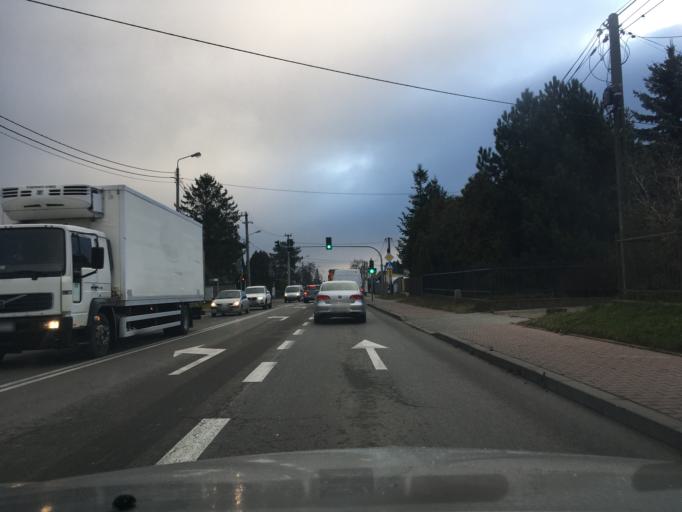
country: PL
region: Masovian Voivodeship
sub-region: Powiat piaseczynski
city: Lesznowola
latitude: 52.0863
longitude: 20.9471
